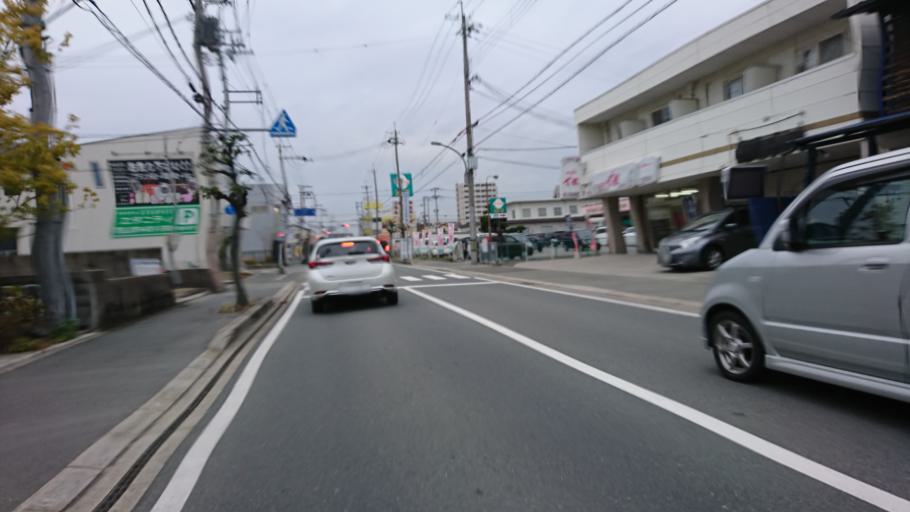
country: JP
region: Hyogo
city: Kakogawacho-honmachi
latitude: 34.7619
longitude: 134.8321
